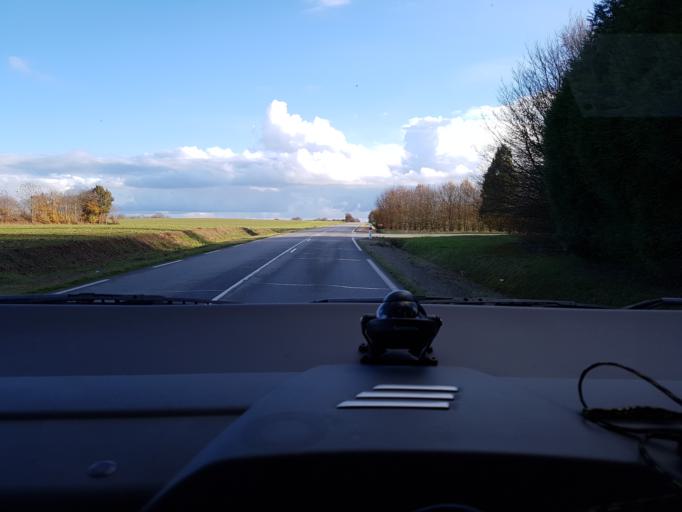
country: FR
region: Brittany
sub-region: Departement d'Ille-et-Vilaine
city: Pire-sur-Seiche
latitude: 48.0132
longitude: -1.3874
